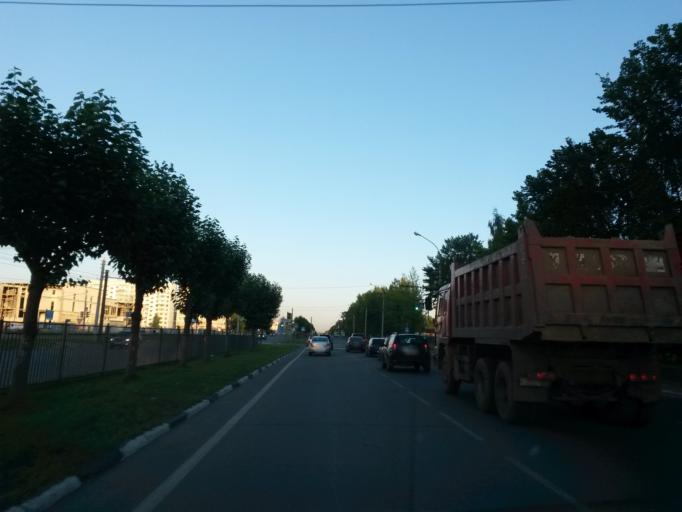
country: RU
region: Jaroslavl
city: Yaroslavl
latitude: 57.6916
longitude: 39.7747
